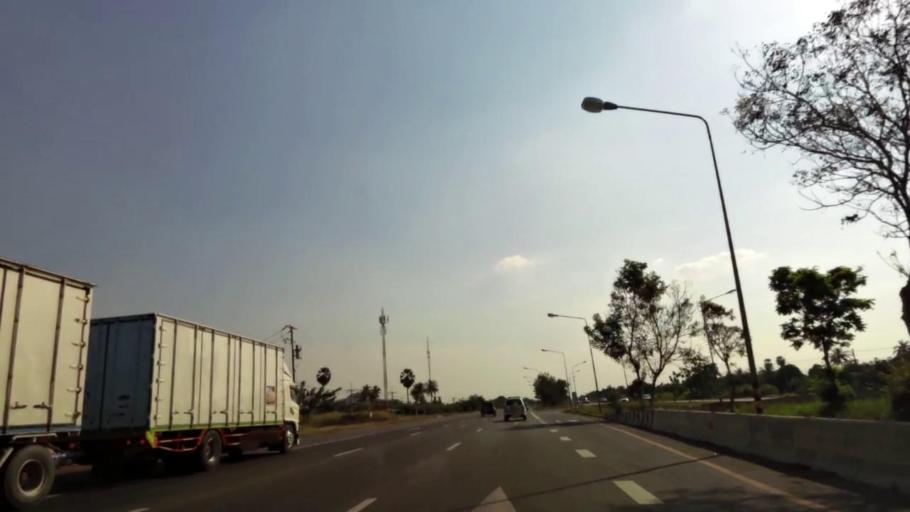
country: TH
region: Ang Thong
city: Chaiyo
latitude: 14.6403
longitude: 100.4746
